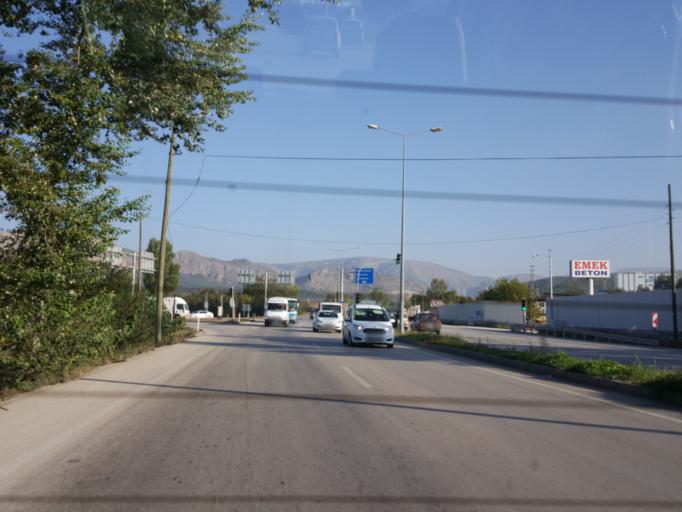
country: TR
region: Amasya
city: Amasya
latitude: 40.5688
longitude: 35.7871
